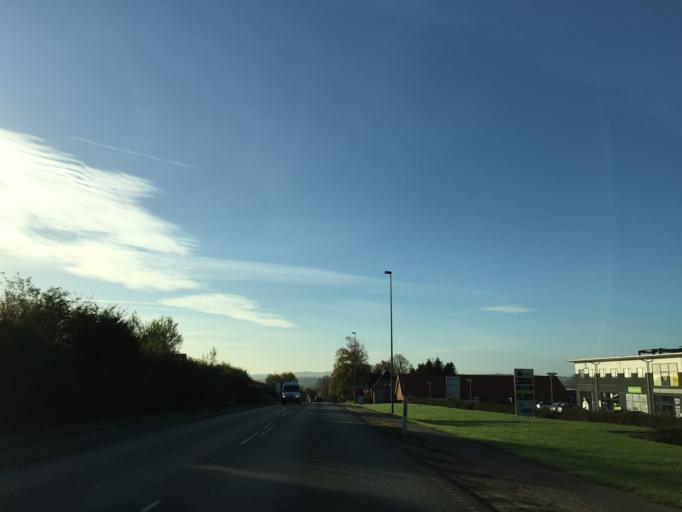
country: DK
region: Central Jutland
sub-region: Skanderborg Kommune
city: Skanderborg
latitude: 56.0470
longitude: 9.9198
